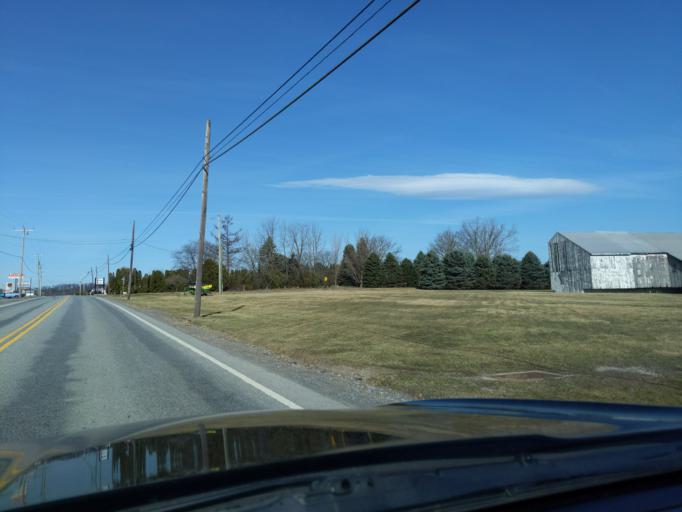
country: US
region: Pennsylvania
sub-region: Blair County
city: Martinsburg
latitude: 40.3086
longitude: -78.2875
